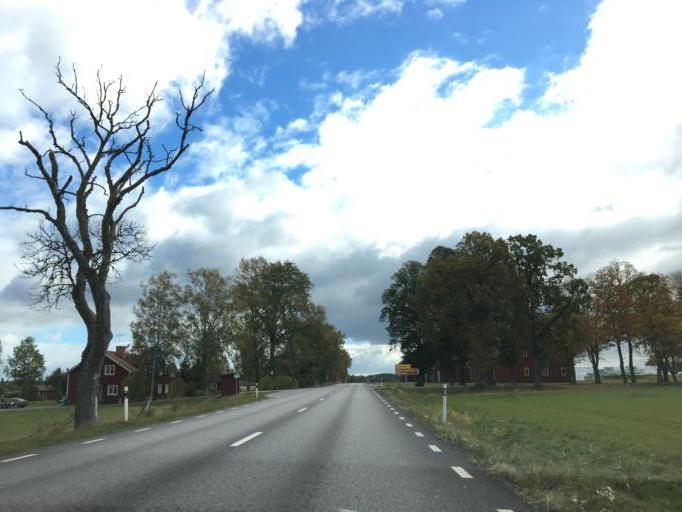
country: SE
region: Soedermanland
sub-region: Katrineholms Kommun
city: Katrineholm
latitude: 58.9441
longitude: 16.3884
